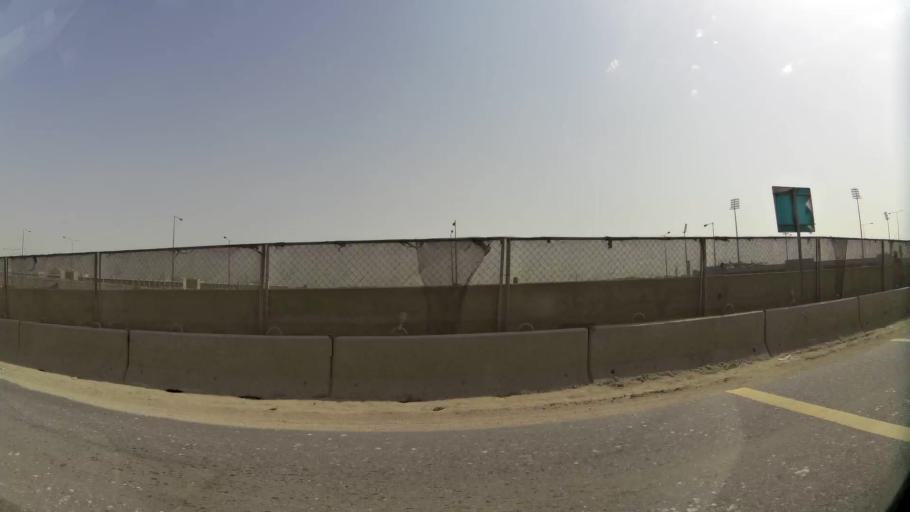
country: QA
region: Al Wakrah
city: Al Wukayr
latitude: 25.1902
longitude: 51.4565
